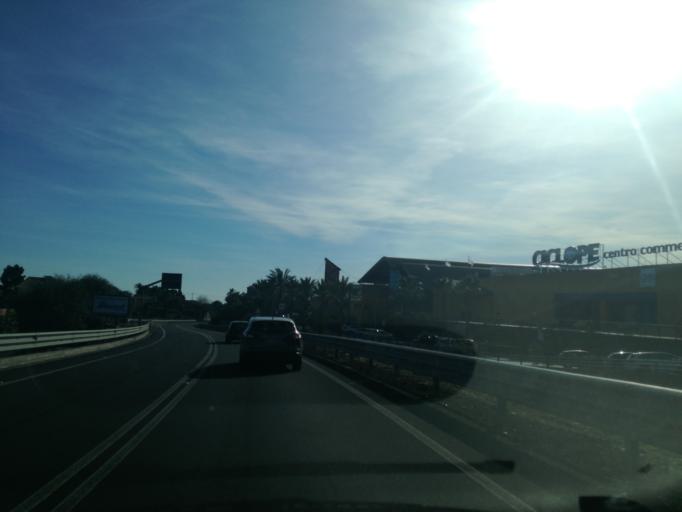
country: IT
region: Sicily
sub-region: Catania
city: Vambolieri
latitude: 37.5970
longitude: 15.1677
